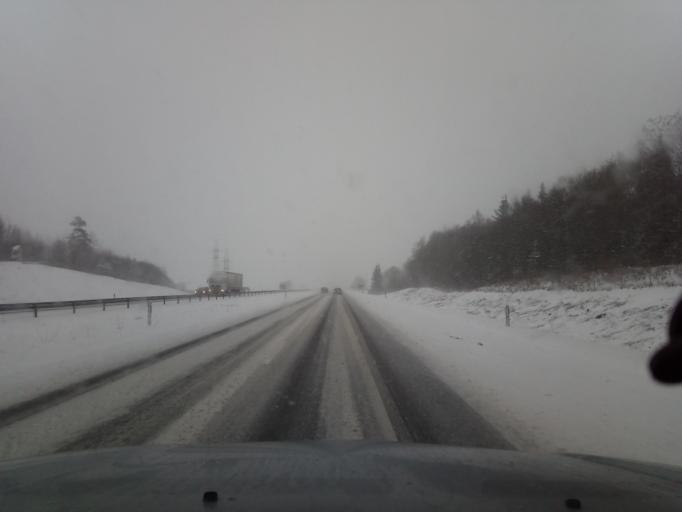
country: LT
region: Vilnius County
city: Pasilaiciai
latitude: 54.7928
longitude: 25.1703
